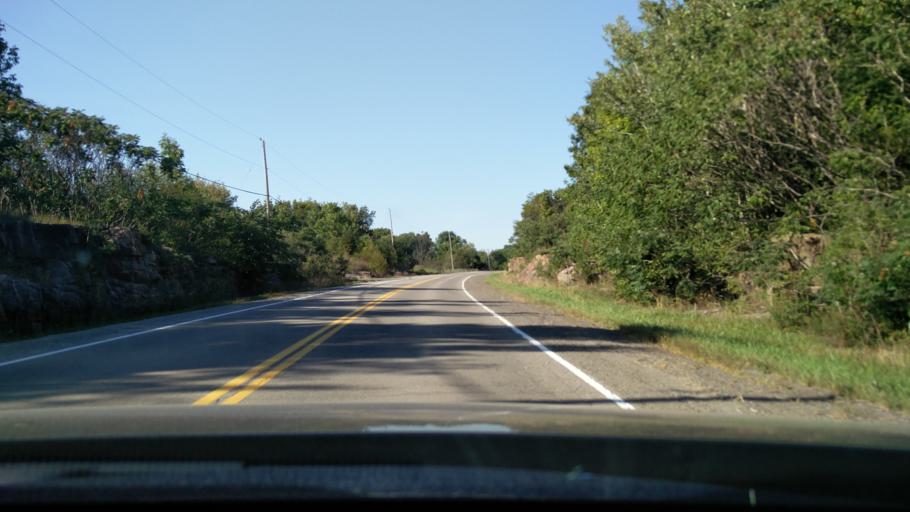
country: CA
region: Ontario
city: Perth
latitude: 44.6950
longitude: -76.4011
